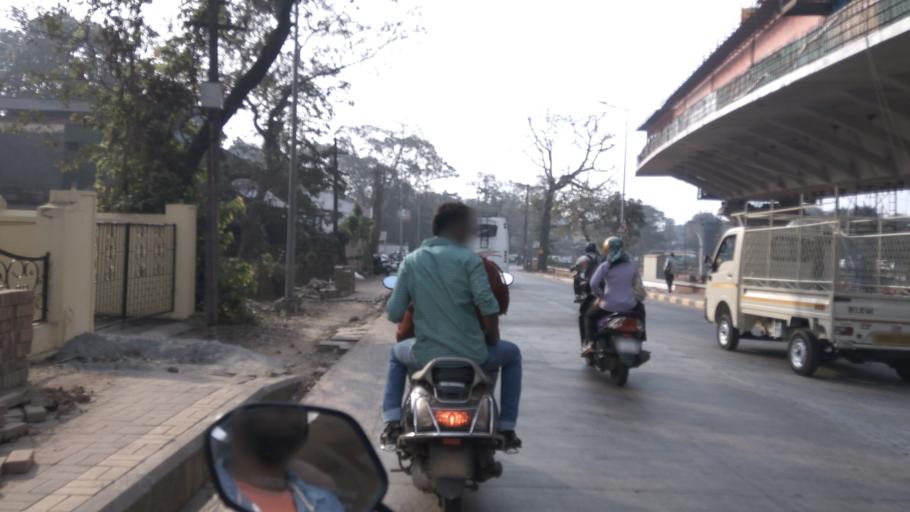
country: IN
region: Goa
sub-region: North Goa
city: Panaji
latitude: 15.5150
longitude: 73.8353
